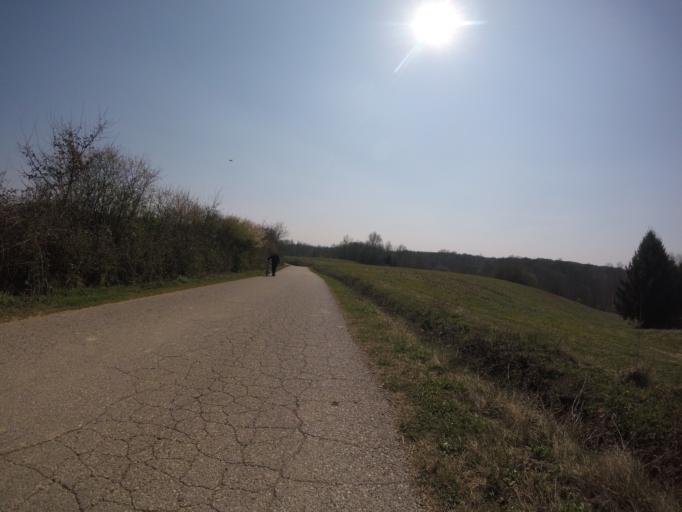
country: HR
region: Grad Zagreb
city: Strmec
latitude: 45.5688
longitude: 15.9212
